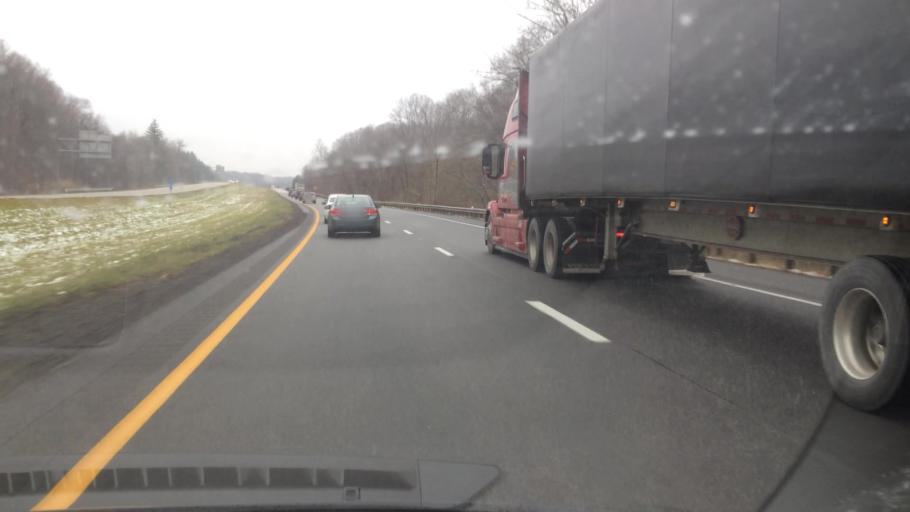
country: US
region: Ohio
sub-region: Summit County
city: Richfield
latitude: 41.2658
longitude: -81.6362
